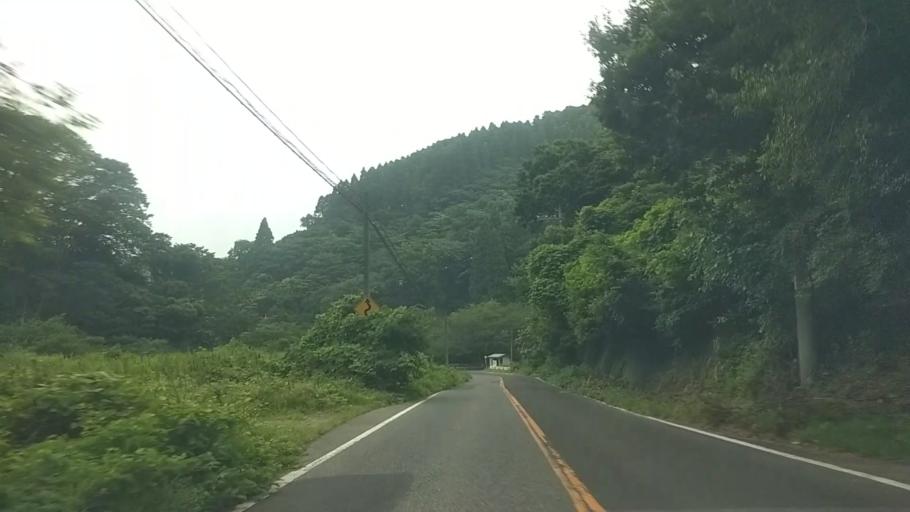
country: JP
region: Chiba
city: Tateyama
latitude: 35.1407
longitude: 139.9016
